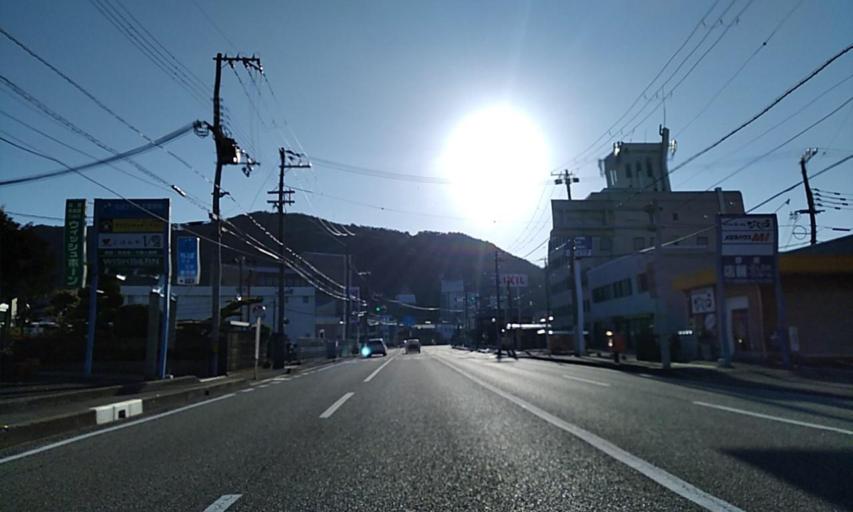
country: JP
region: Wakayama
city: Kainan
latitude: 34.1863
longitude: 135.1831
